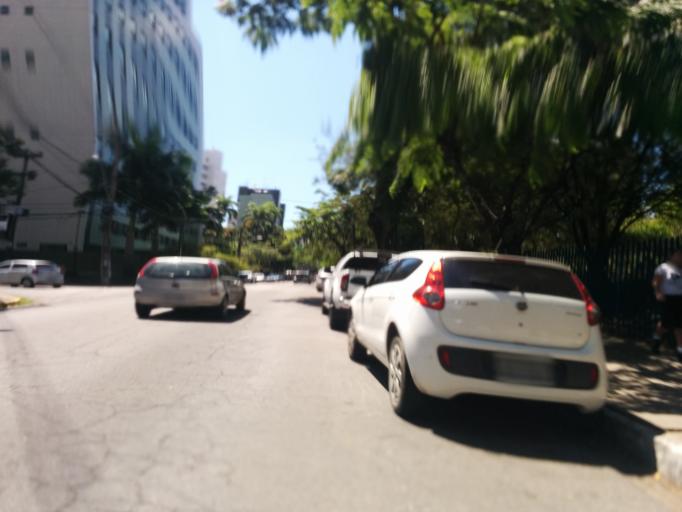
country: BR
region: Pernambuco
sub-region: Recife
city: Recife
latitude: -8.0355
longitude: -34.9045
